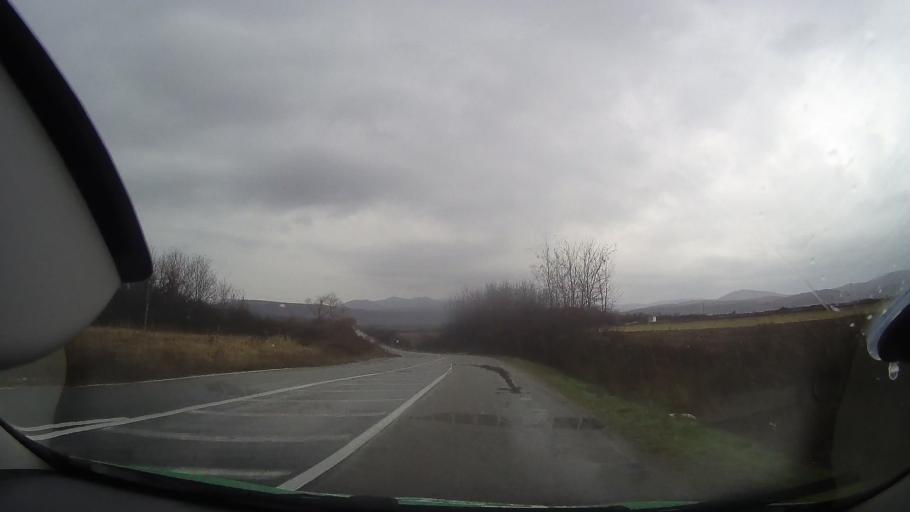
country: RO
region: Bihor
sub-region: Comuna Soimi
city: Soimi
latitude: 46.6954
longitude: 22.0944
